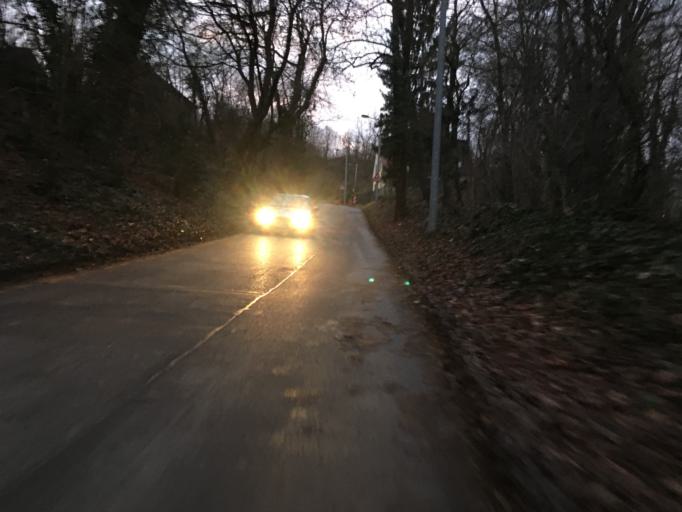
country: DE
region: Baden-Wuerttemberg
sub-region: Regierungsbezirk Stuttgart
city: Kornwestheim
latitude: 48.8391
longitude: 9.1993
